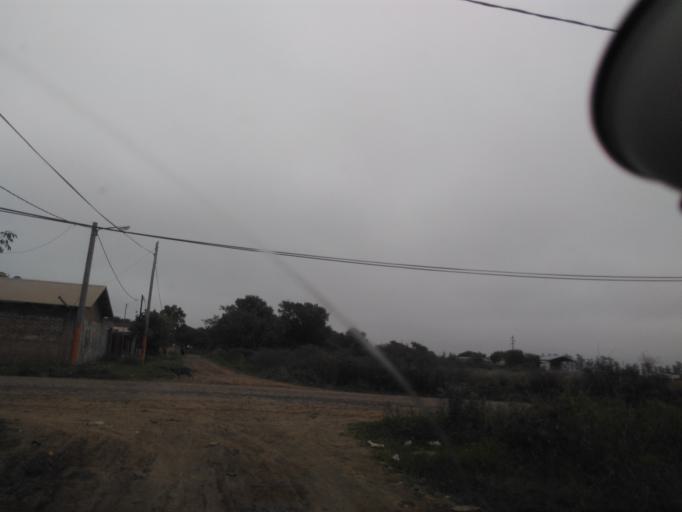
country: AR
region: Chaco
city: Fontana
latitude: -27.4004
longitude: -58.9937
